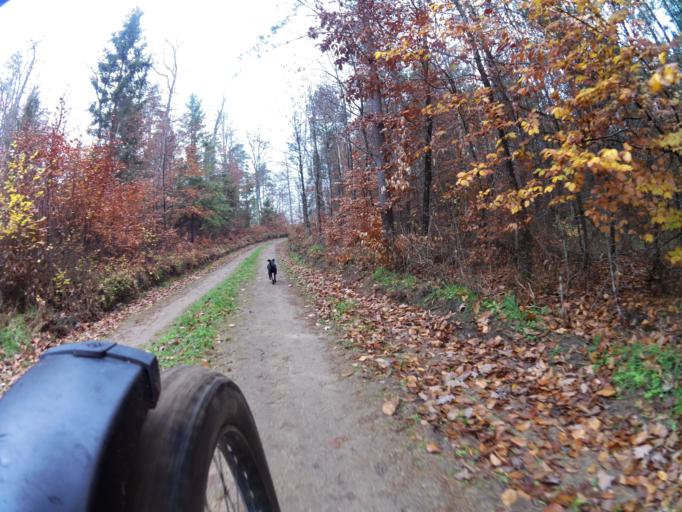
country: PL
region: Pomeranian Voivodeship
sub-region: Powiat wejherowski
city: Orle
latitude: 54.6978
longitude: 18.1564
